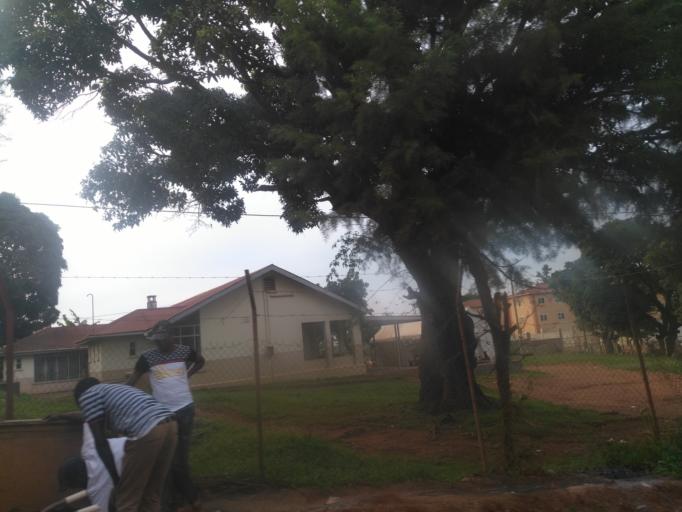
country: UG
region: Central Region
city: Kampala Central Division
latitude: 0.3437
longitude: 32.5785
